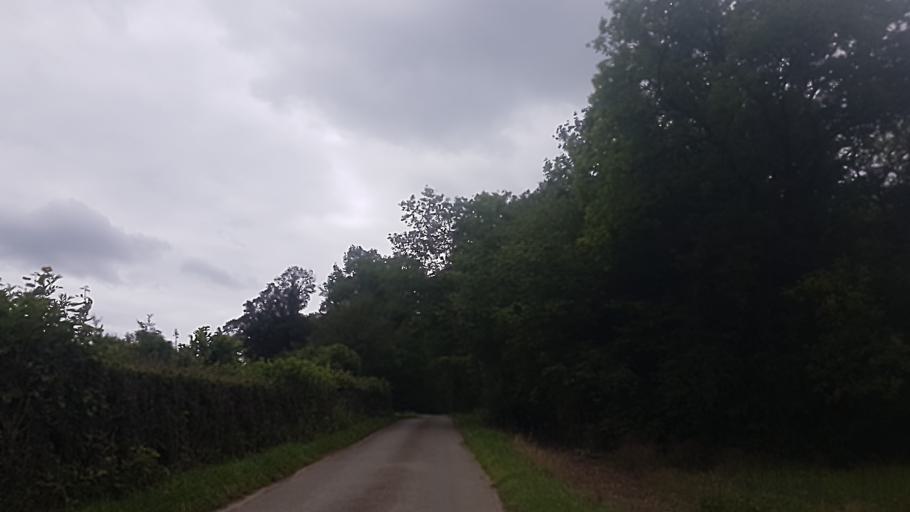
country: BE
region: Wallonia
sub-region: Province de Namur
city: Philippeville
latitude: 50.1026
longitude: 4.5882
